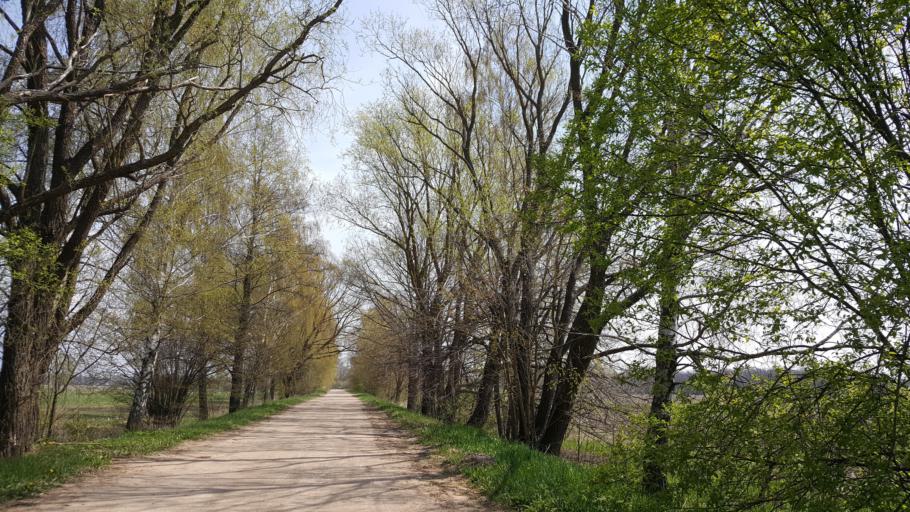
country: BY
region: Brest
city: Zhabinka
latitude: 52.2948
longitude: 23.9206
